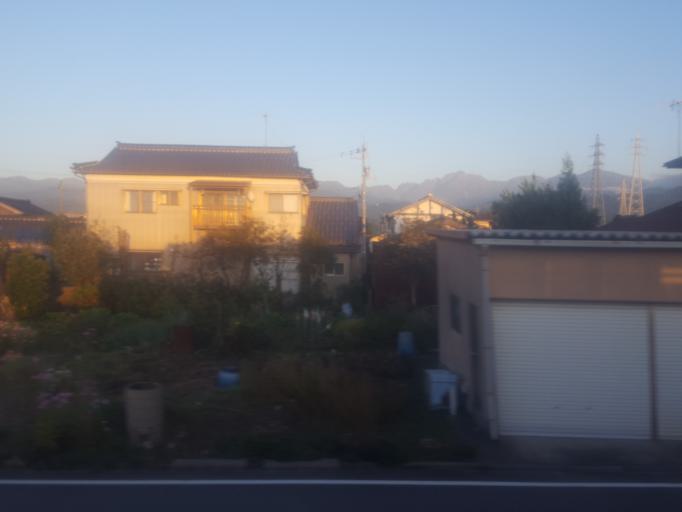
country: JP
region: Toyama
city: Kamiichi
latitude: 36.6911
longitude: 137.3180
